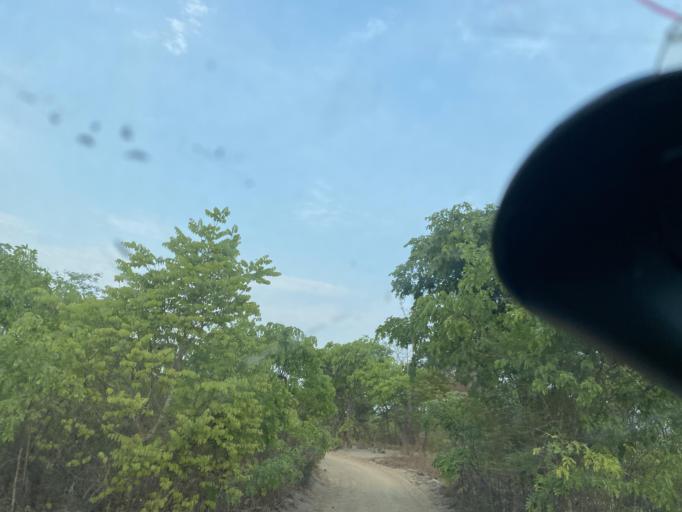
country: ZM
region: Lusaka
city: Chongwe
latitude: -15.2081
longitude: 28.5076
